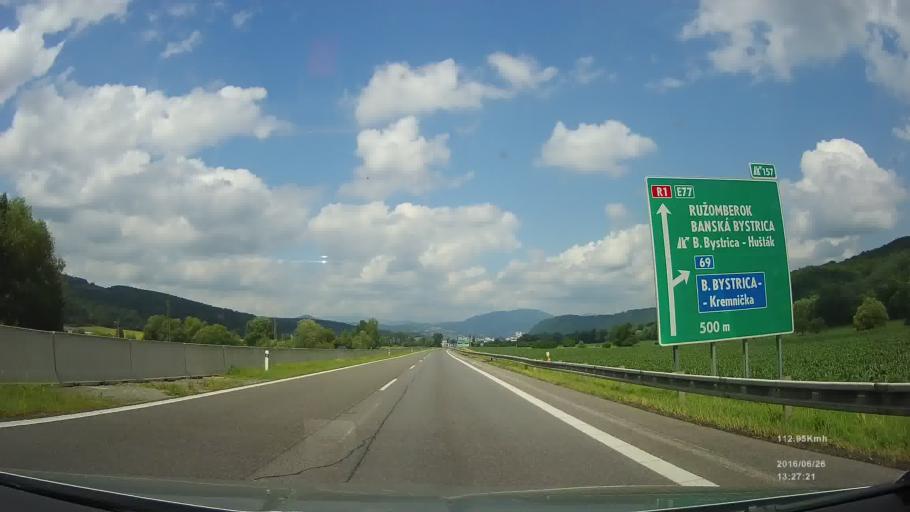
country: SK
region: Banskobystricky
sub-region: Okres Banska Bystrica
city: Banska Bystrica
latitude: 48.6817
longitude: 19.1321
